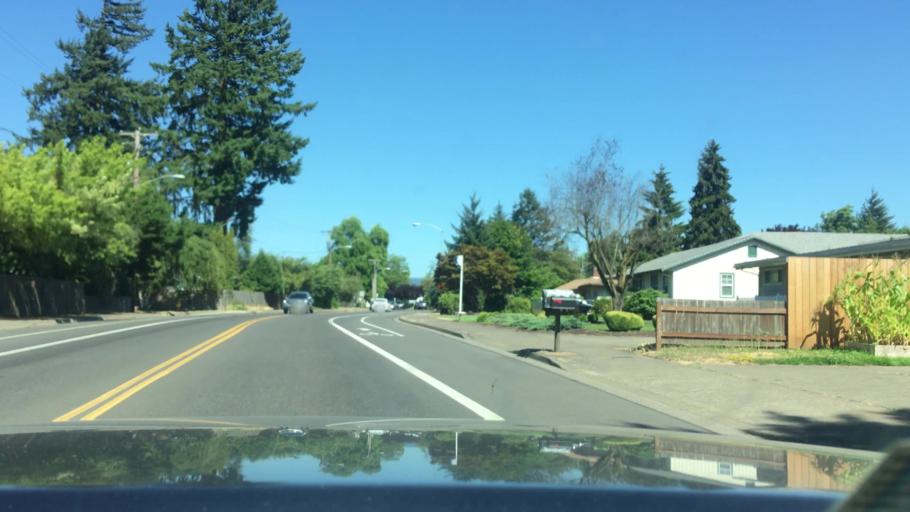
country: US
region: Oregon
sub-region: Lane County
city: Eugene
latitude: 44.0928
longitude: -123.0902
